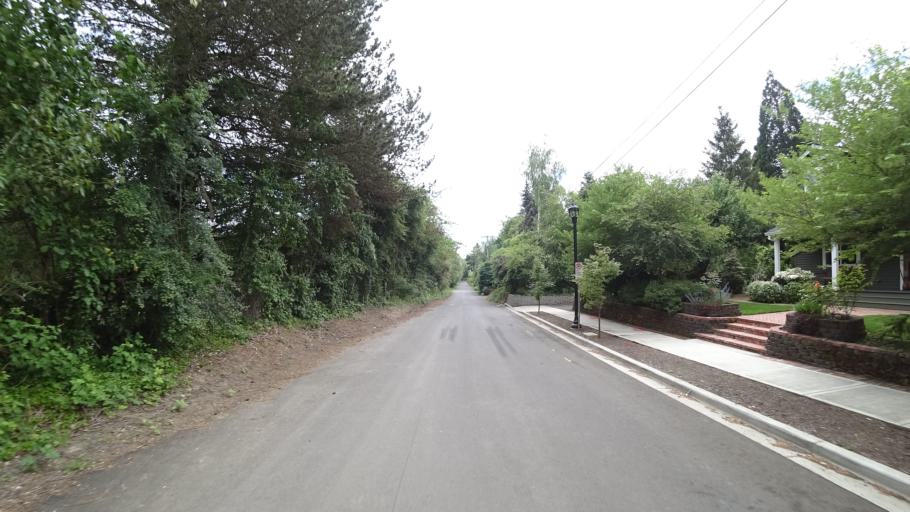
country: US
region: Oregon
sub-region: Washington County
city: Raleigh Hills
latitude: 45.4726
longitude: -122.7653
